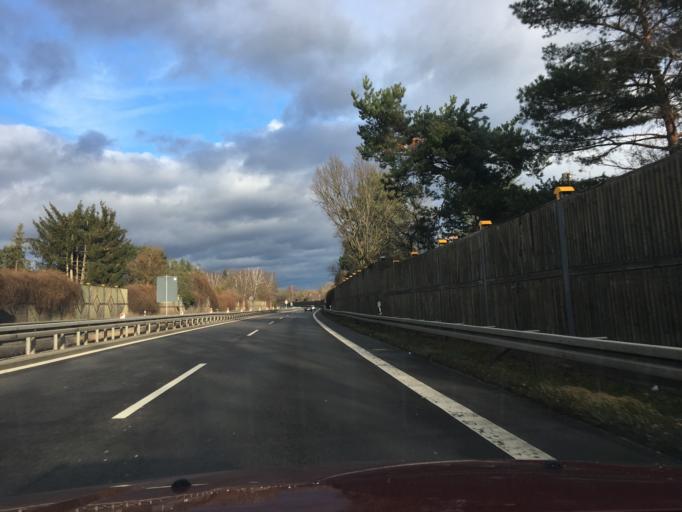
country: DE
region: Berlin
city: Bohnsdorf
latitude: 52.3881
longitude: 13.5642
